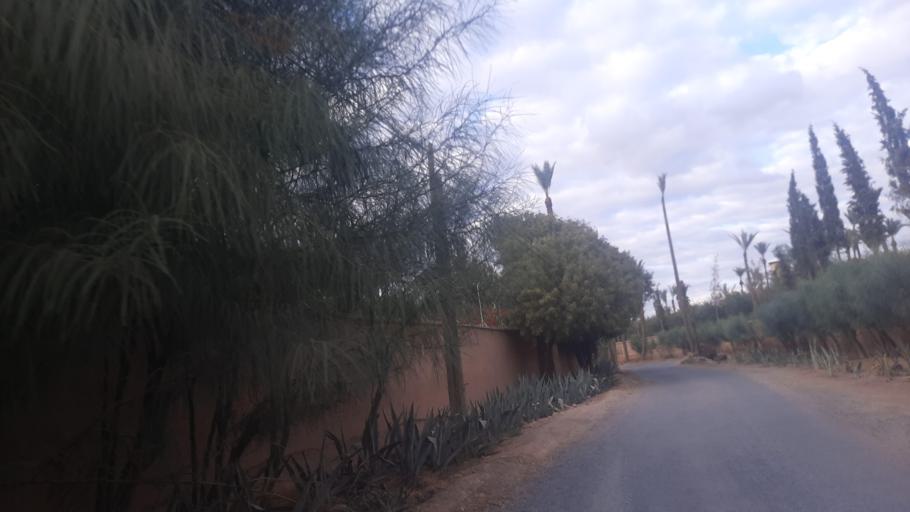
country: MA
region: Marrakech-Tensift-Al Haouz
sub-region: Marrakech
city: Marrakesh
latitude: 31.6743
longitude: -7.9533
